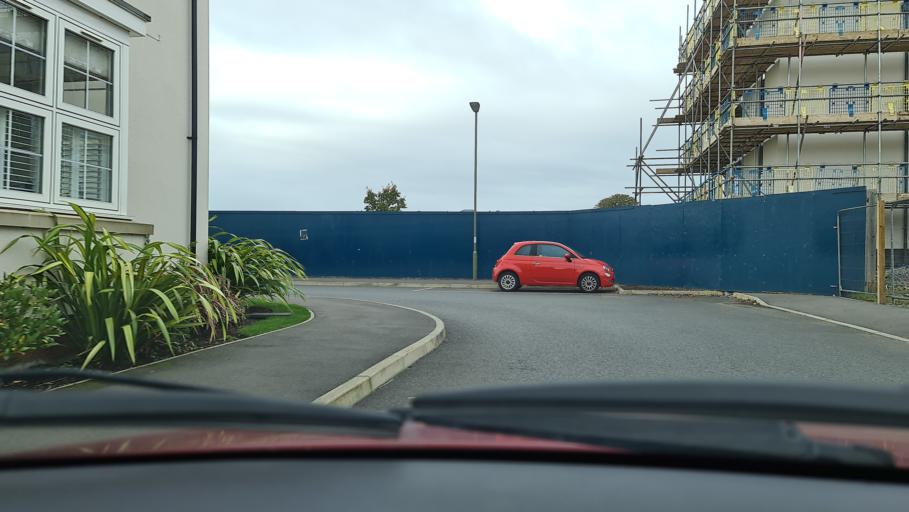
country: GB
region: England
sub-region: Oxfordshire
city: Somerton
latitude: 51.9275
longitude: -1.2529
